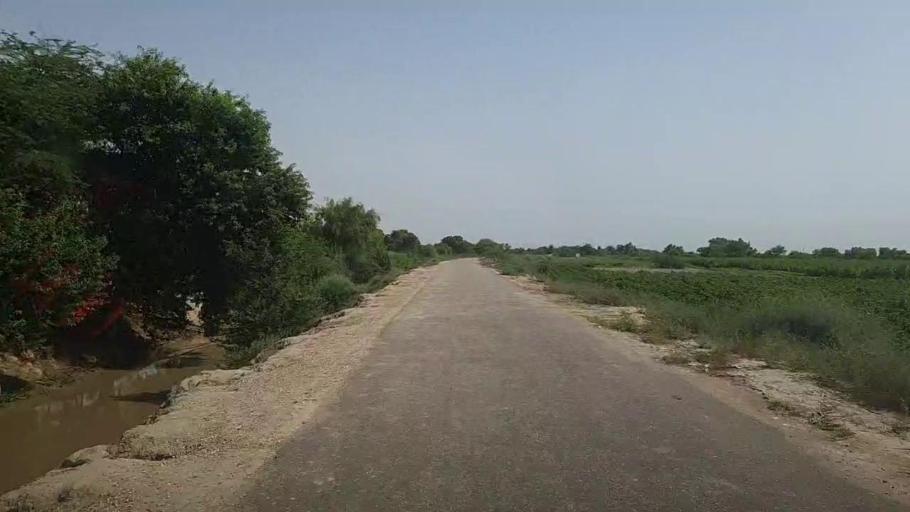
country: PK
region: Sindh
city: Pad Idan
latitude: 26.8035
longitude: 68.3325
